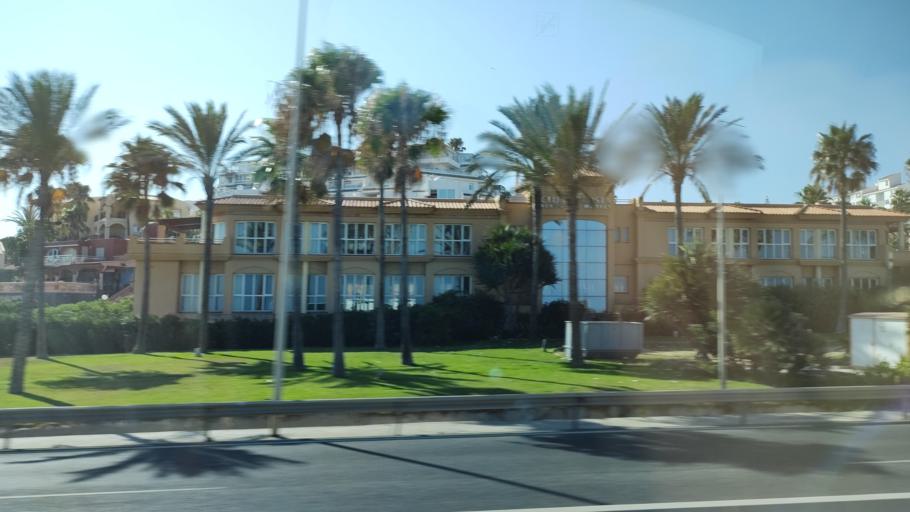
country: ES
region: Andalusia
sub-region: Provincia de Malaga
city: Fuengirola
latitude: 36.5147
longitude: -4.6332
